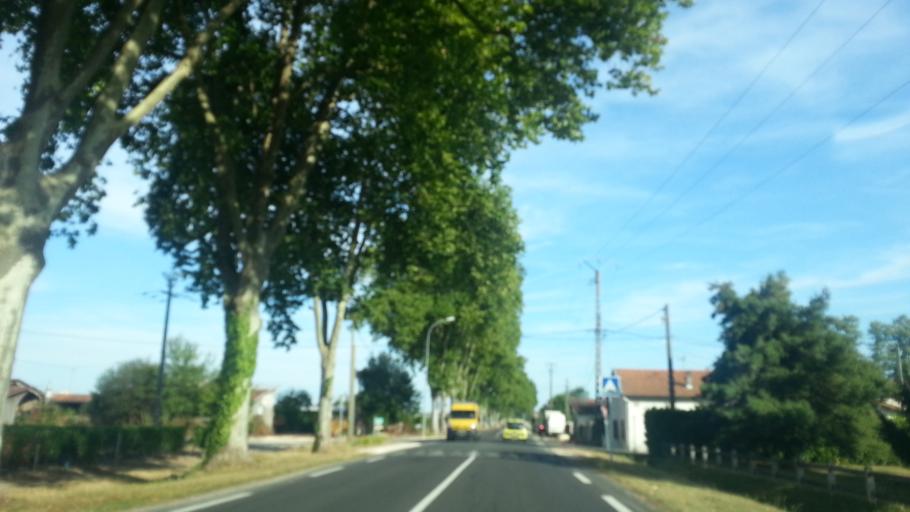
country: FR
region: Aquitaine
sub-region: Departement de la Gironde
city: Portets
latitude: 44.6786
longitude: -0.4036
